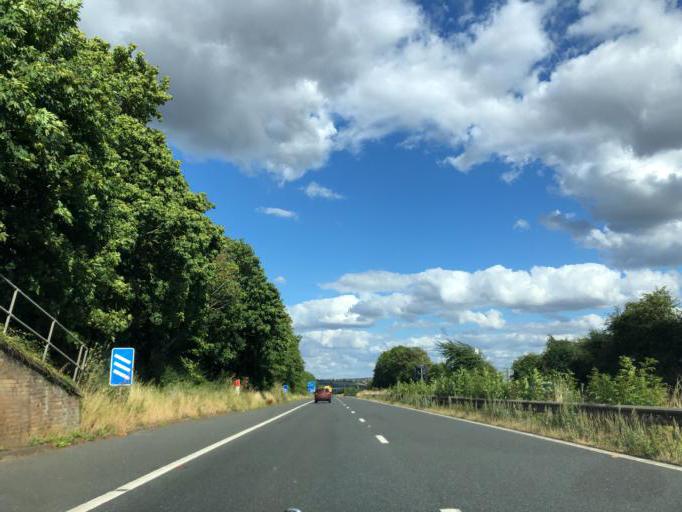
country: GB
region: England
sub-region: Warwickshire
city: Dunchurch
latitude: 52.3338
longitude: -1.2936
